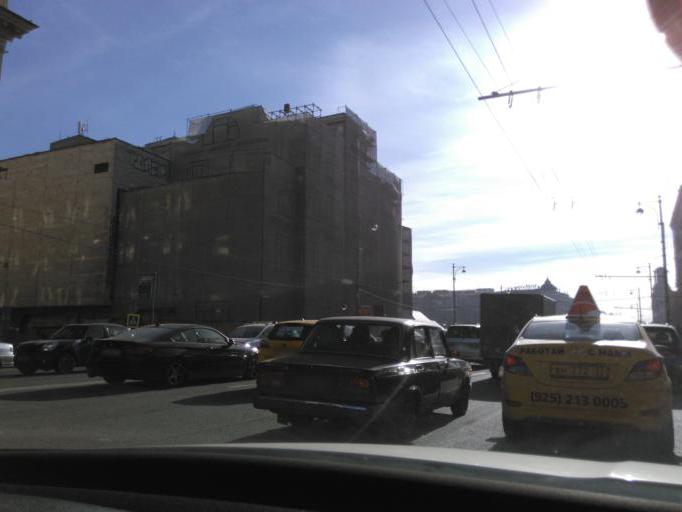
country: RU
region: Moscow
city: Moscow
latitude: 55.7664
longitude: 37.6021
